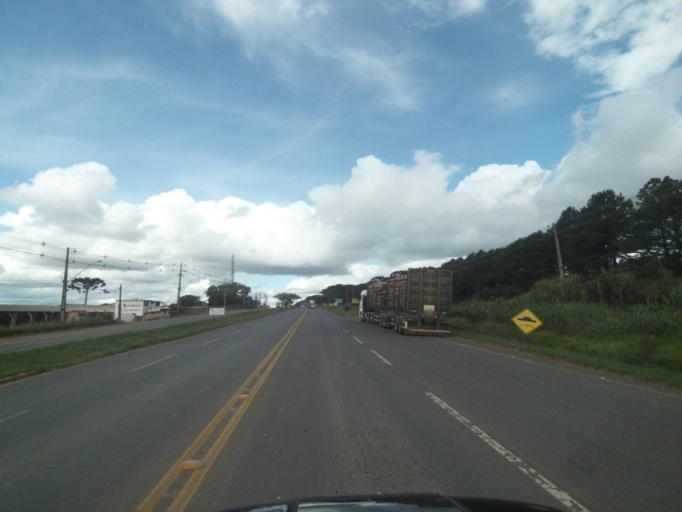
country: BR
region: Parana
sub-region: Telemaco Borba
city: Telemaco Borba
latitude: -24.3799
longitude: -50.6698
